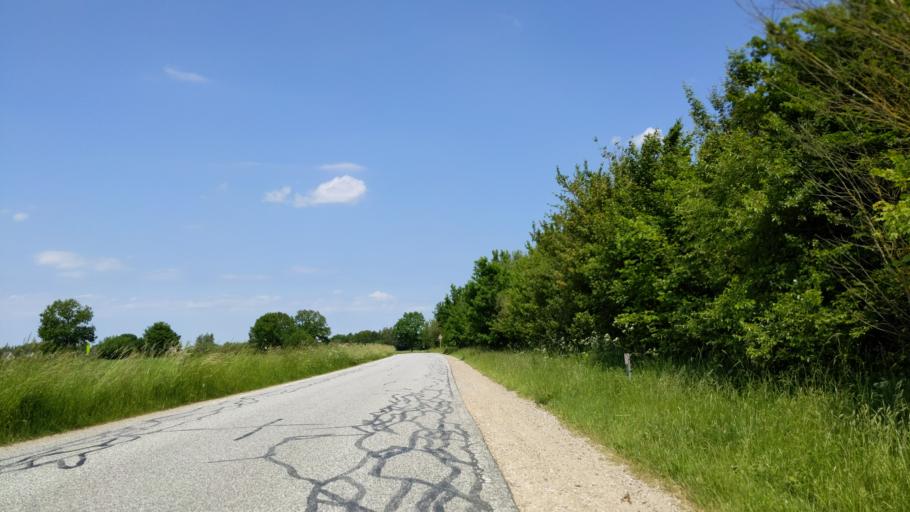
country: DE
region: Schleswig-Holstein
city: Krummesse
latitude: 53.8245
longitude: 10.6627
